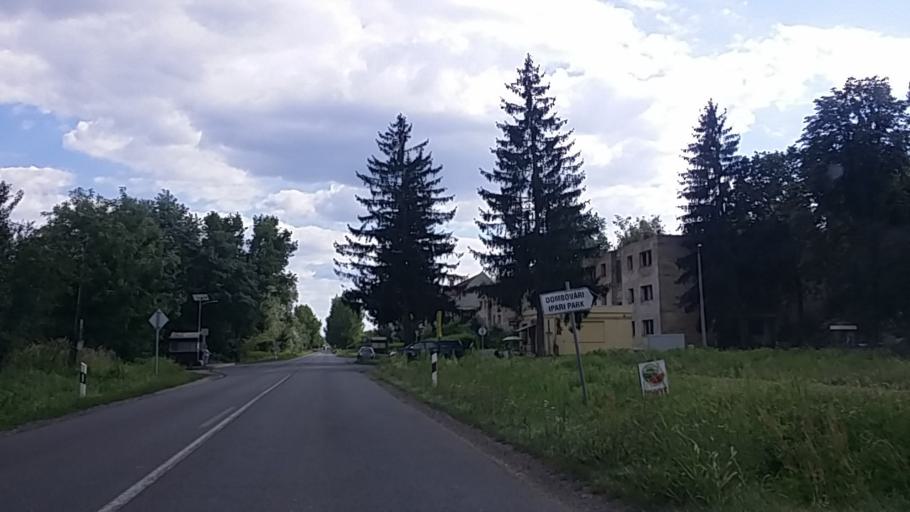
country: HU
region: Tolna
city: Dombovar
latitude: 46.3518
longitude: 18.1266
